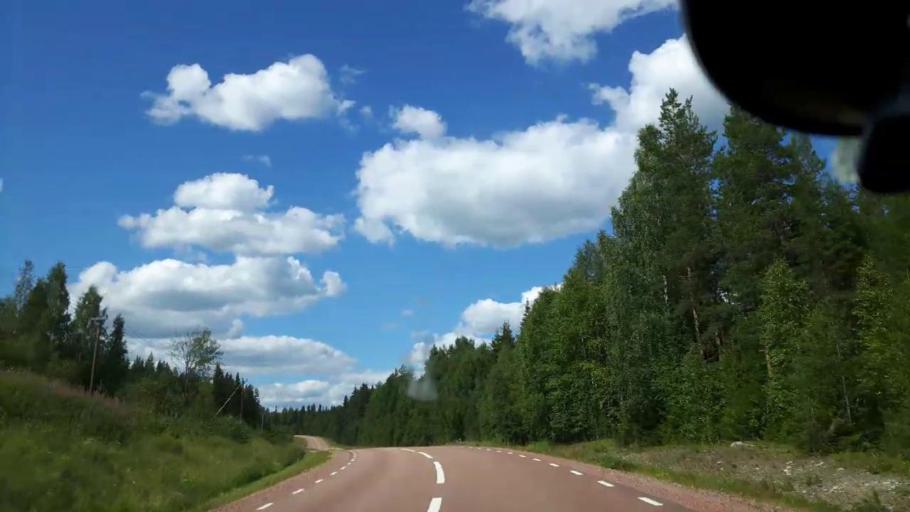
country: SE
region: Jaemtland
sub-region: Ragunda Kommun
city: Hammarstrand
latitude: 63.0157
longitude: 16.6189
